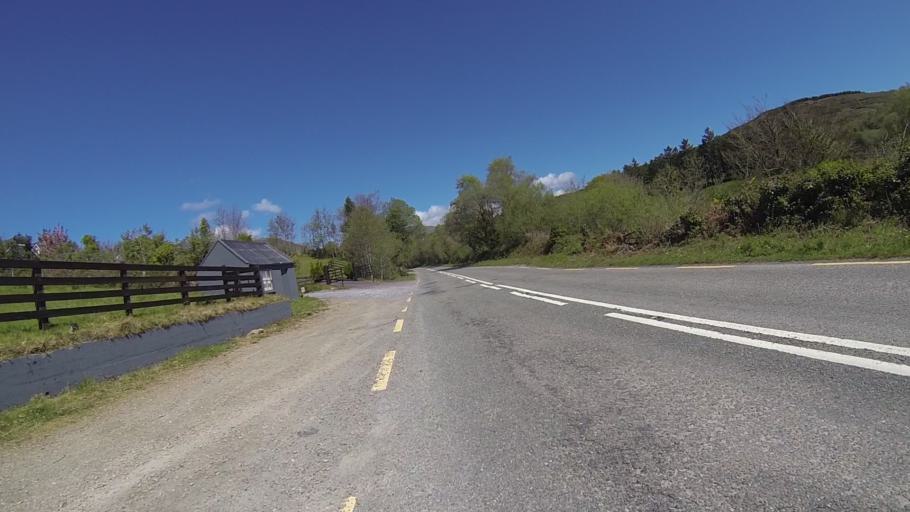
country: IE
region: Munster
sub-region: Ciarrai
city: Kenmare
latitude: 51.8982
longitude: -9.6000
